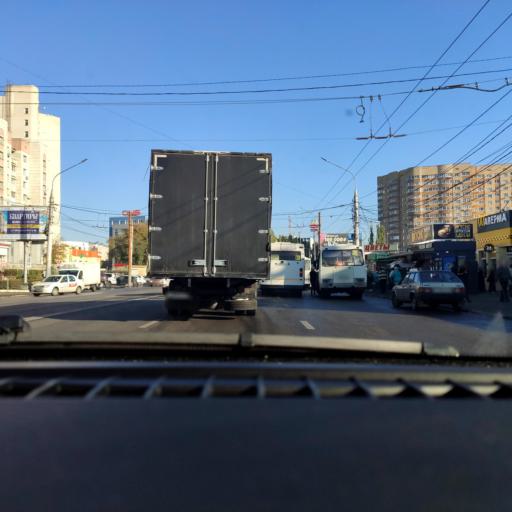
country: RU
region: Voronezj
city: Voronezh
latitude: 51.6713
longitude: 39.2521
